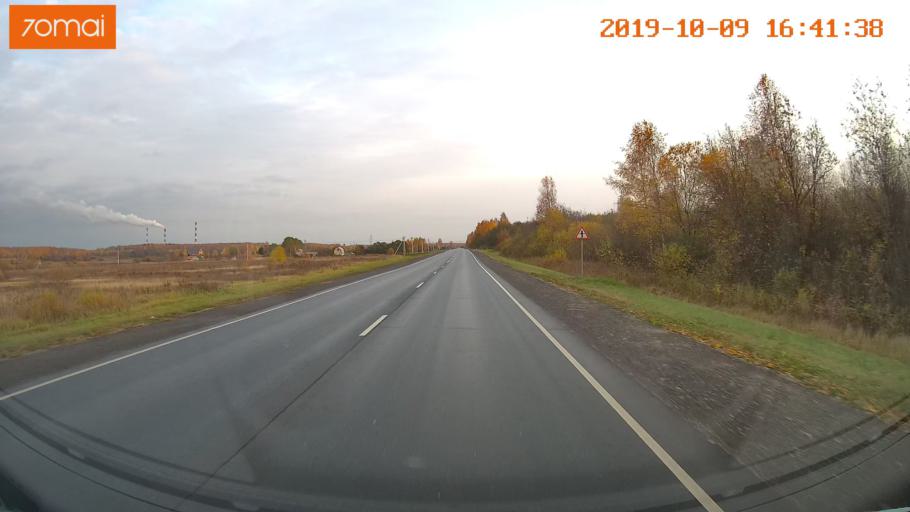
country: RU
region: Kostroma
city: Volgorechensk
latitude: 57.4711
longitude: 41.0847
